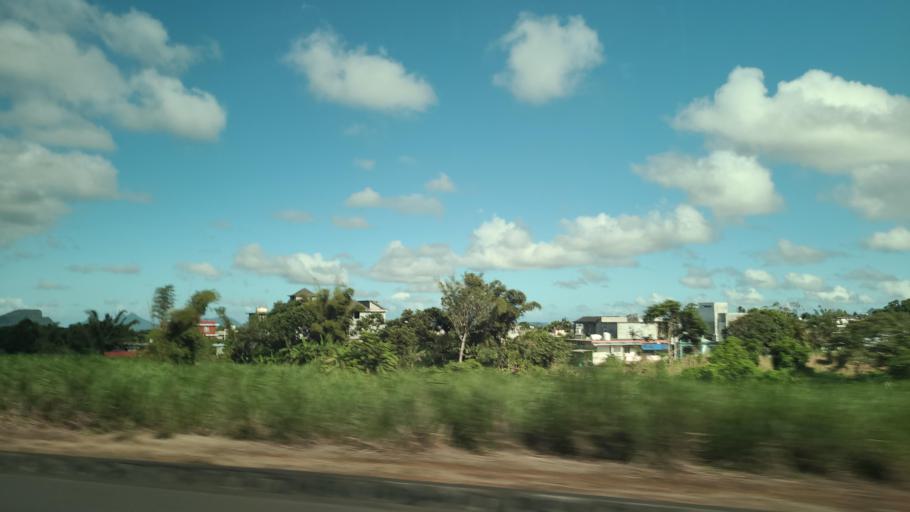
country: MU
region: Moka
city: Quartier Militaire
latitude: -20.2422
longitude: 57.5957
